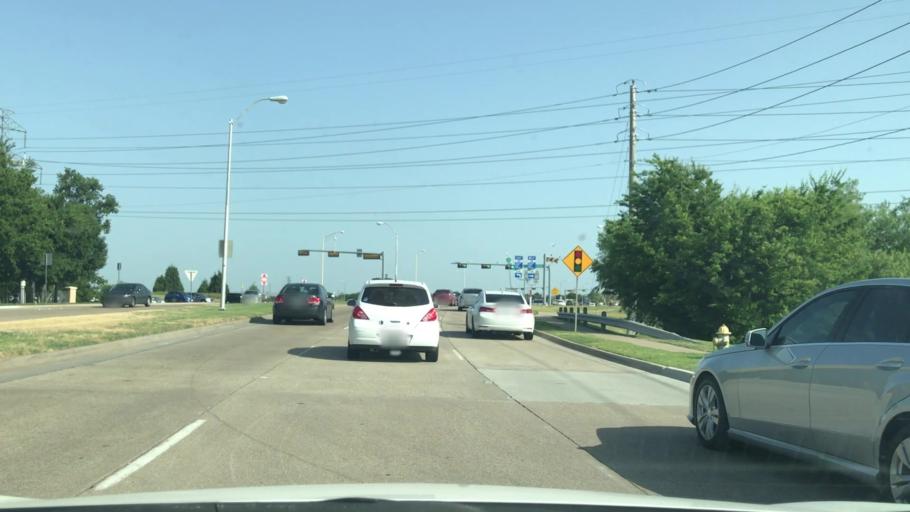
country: US
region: Texas
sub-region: Collin County
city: Plano
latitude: 33.0052
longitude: -96.7492
